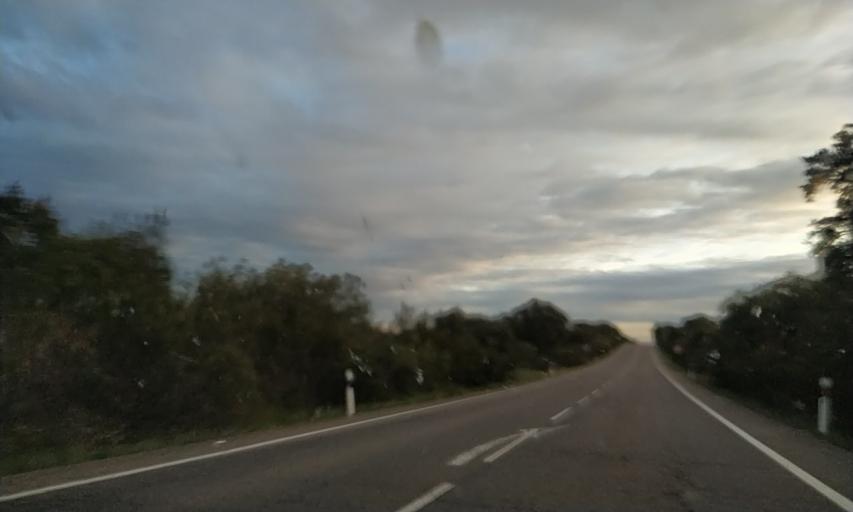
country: ES
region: Extremadura
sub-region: Provincia de Badajoz
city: Puebla de Obando
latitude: 39.1559
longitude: -6.6453
